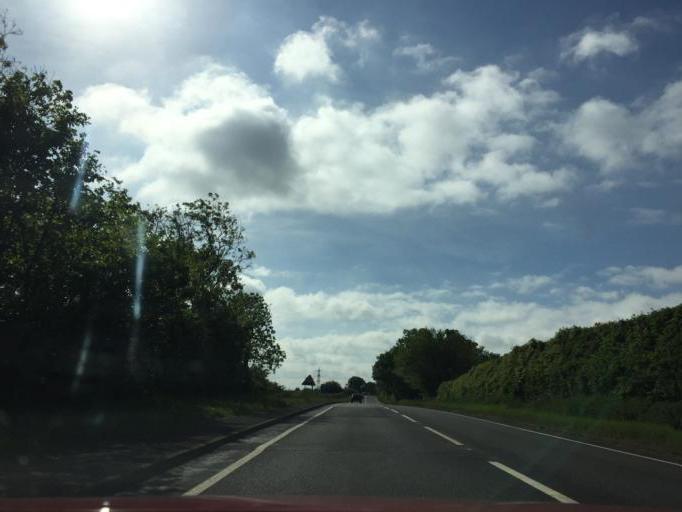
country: GB
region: England
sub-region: Northamptonshire
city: Towcester
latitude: 52.1104
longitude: -0.9498
